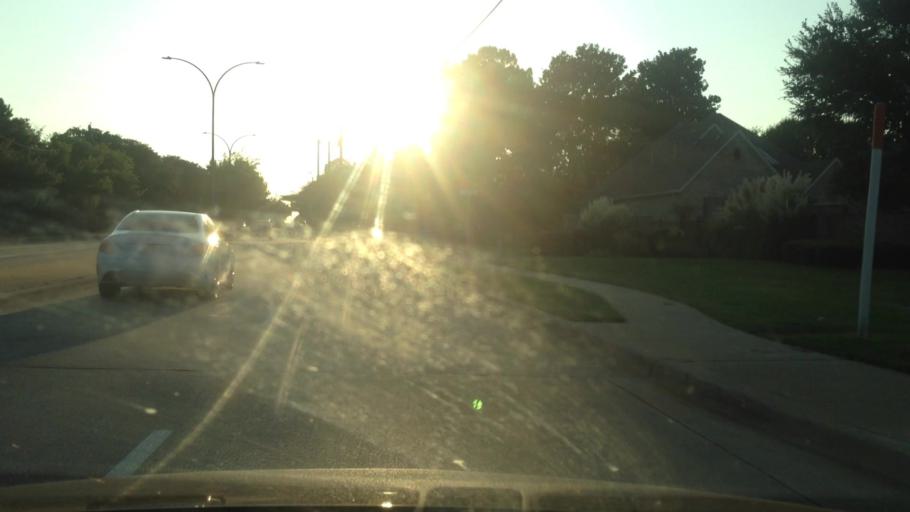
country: US
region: Texas
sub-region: Tarrant County
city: Dalworthington Gardens
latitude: 32.6492
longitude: -97.1674
